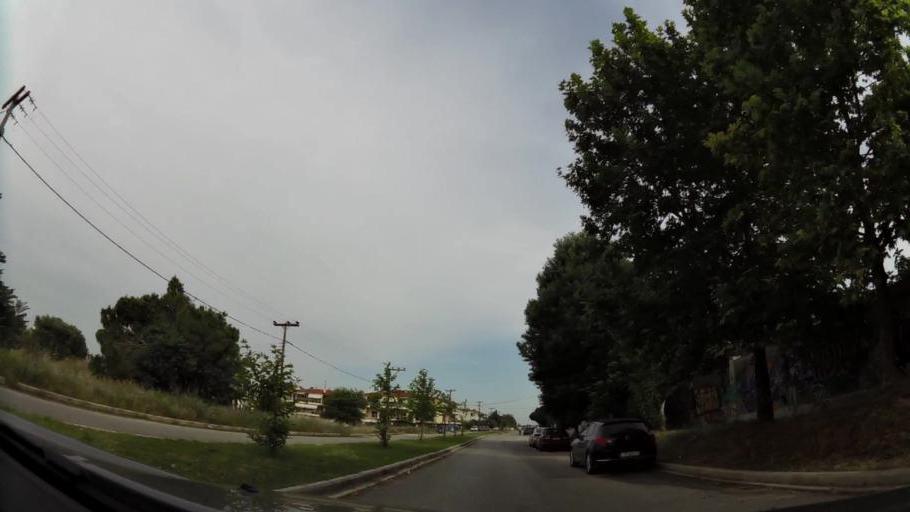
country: GR
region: Central Macedonia
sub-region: Nomos Thessalonikis
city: Thermi
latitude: 40.5472
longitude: 23.0140
